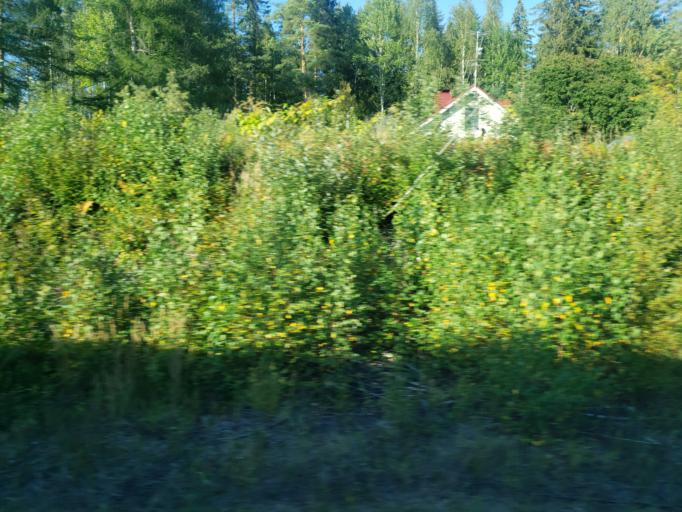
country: FI
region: South Karelia
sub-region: Lappeenranta
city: Lappeenranta
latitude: 60.9096
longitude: 28.1334
